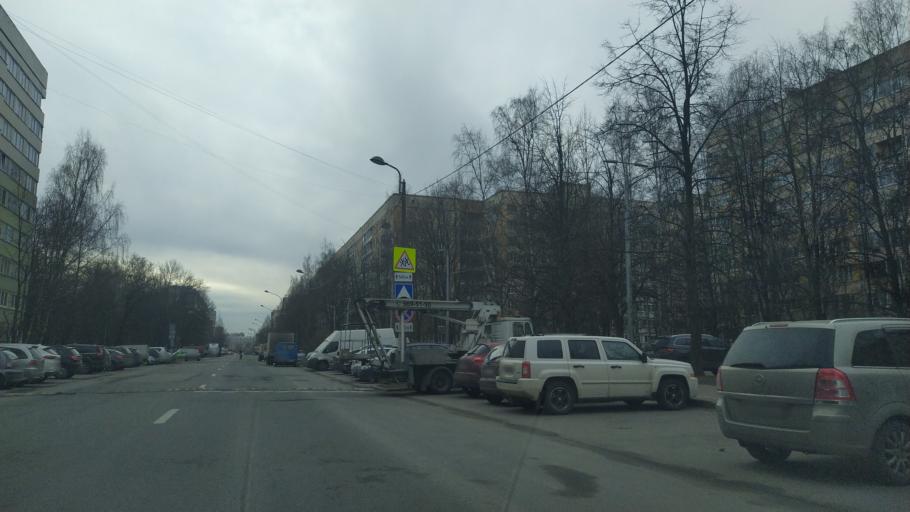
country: RU
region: St.-Petersburg
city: Grazhdanka
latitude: 60.0293
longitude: 30.4256
